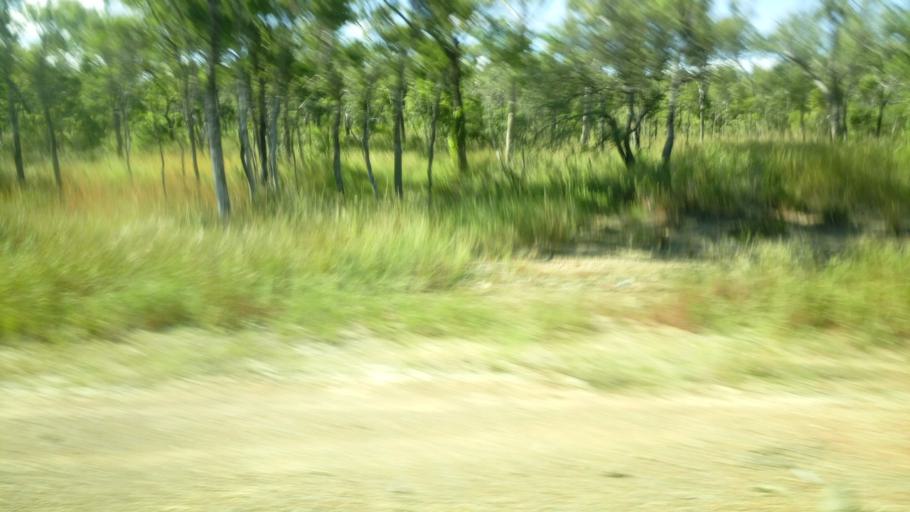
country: AU
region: Queensland
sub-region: Cairns
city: Port Douglas
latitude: -16.5201
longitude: 145.0942
